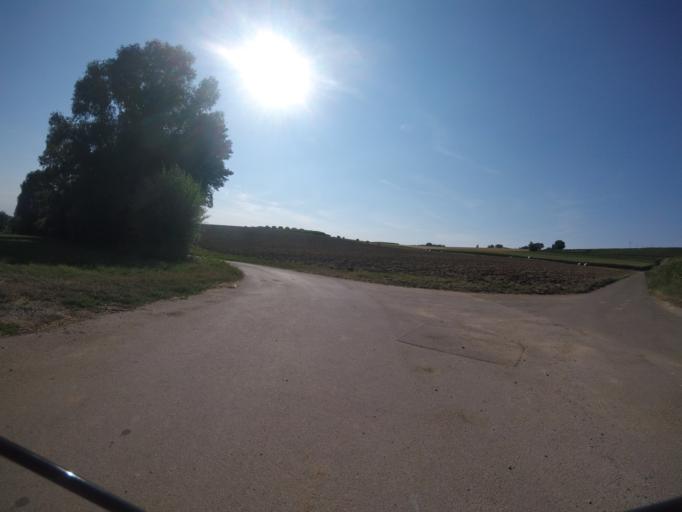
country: DE
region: Baden-Wuerttemberg
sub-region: Regierungsbezirk Stuttgart
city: Kirchberg an der Murr
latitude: 48.9600
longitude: 9.3154
